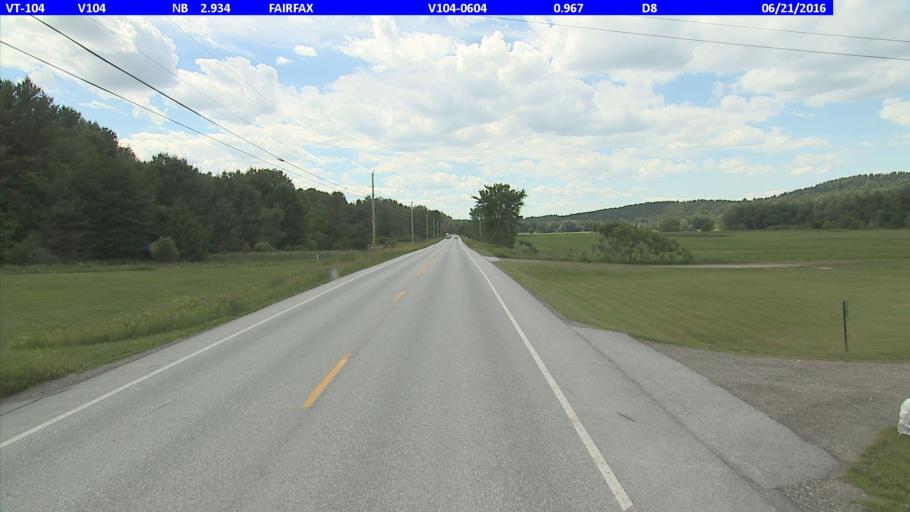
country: US
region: Vermont
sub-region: Chittenden County
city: Jericho
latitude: 44.6429
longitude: -72.9439
